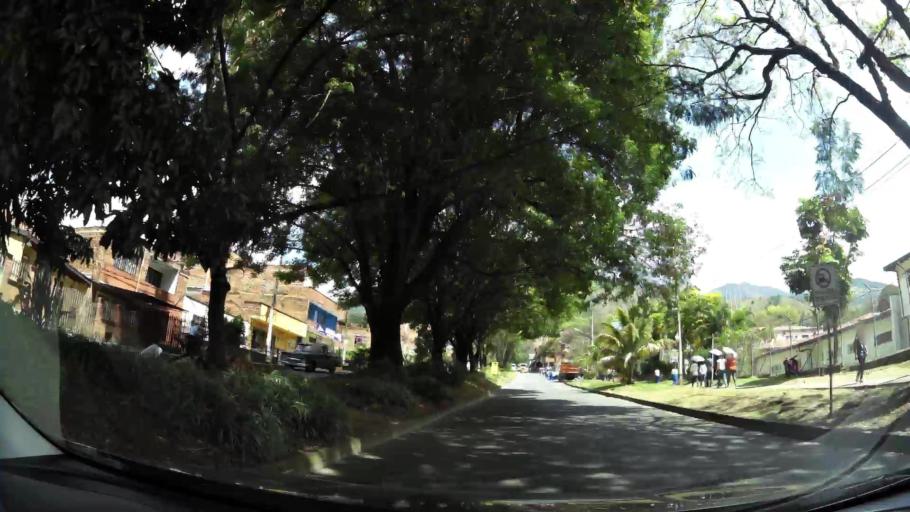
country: CO
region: Antioquia
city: Bello
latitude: 6.3422
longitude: -75.5485
